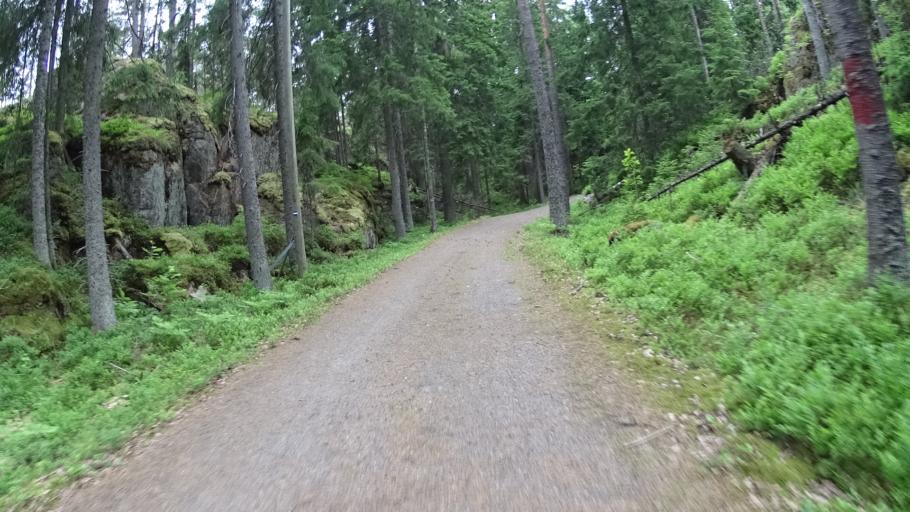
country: FI
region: Uusimaa
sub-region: Helsinki
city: Espoo
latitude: 60.2940
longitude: 24.5718
